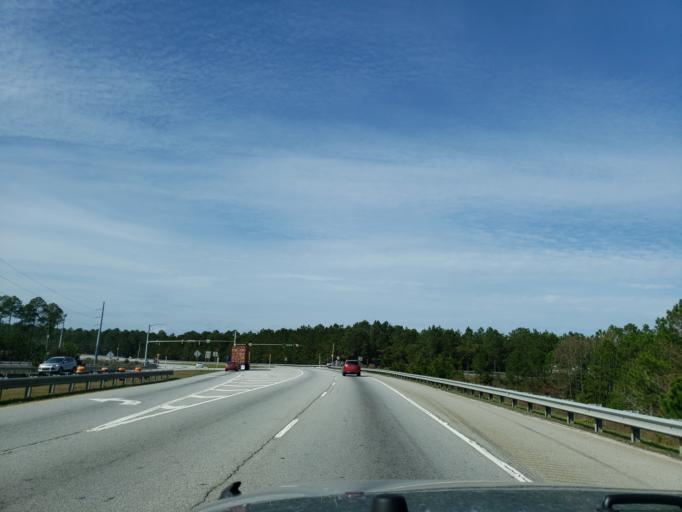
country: US
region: Georgia
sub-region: Chatham County
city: Port Wentworth
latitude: 32.1670
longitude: -81.2163
